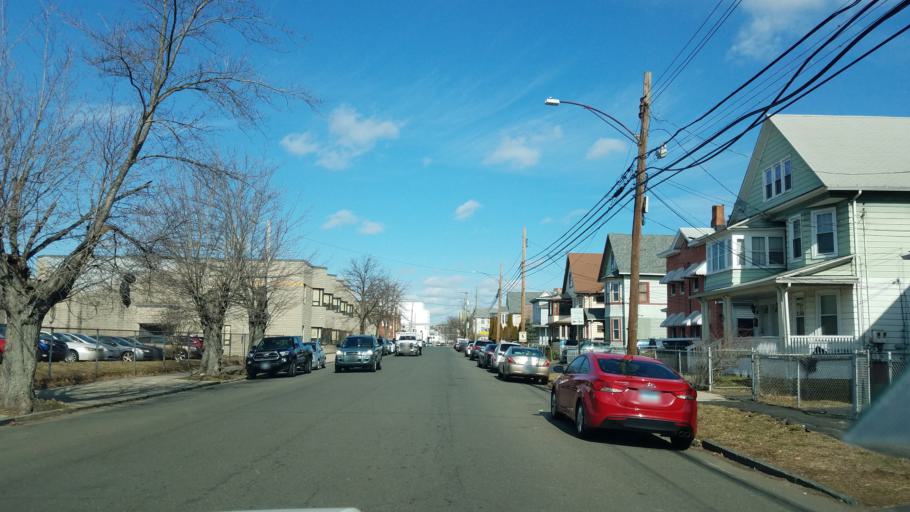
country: US
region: Connecticut
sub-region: Fairfield County
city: Stratford
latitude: 41.1769
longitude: -73.1641
